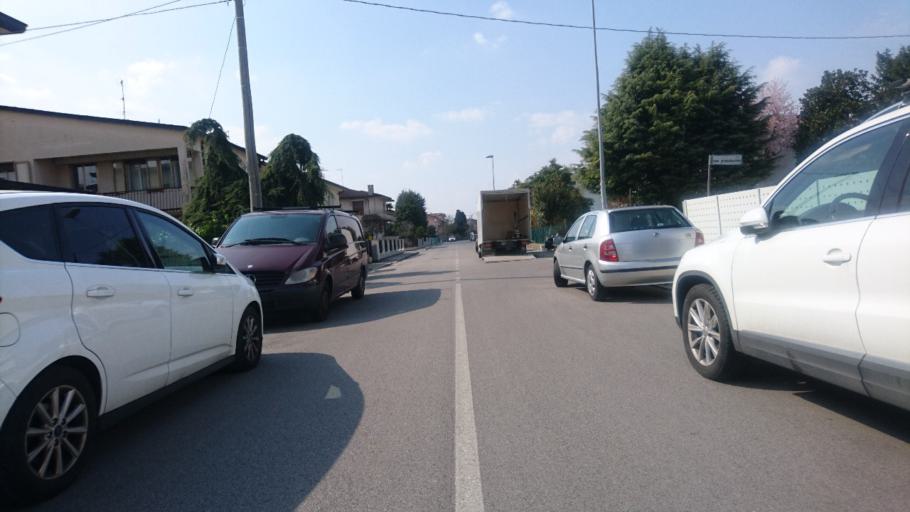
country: IT
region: Veneto
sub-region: Provincia di Padova
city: Mandriola-Sant'Agostino
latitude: 45.3579
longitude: 11.8676
